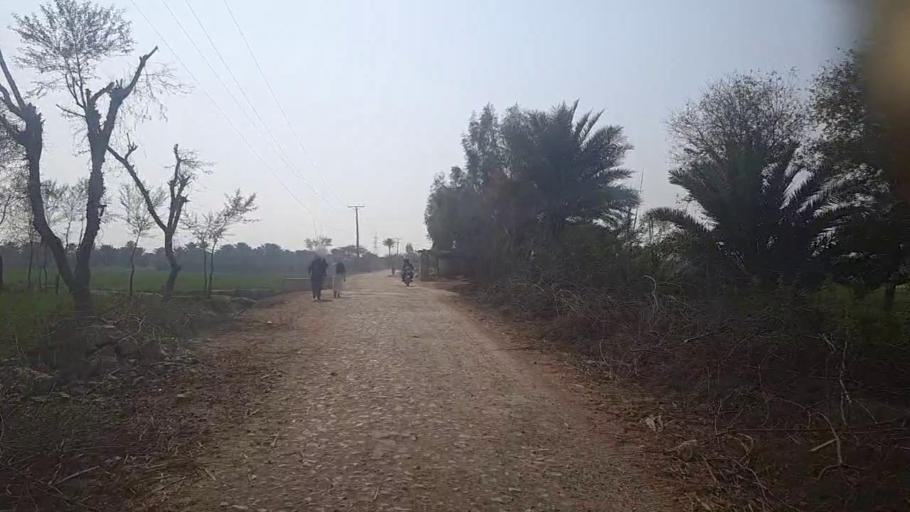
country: PK
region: Sindh
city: Kot Diji
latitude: 27.3609
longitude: 68.7425
